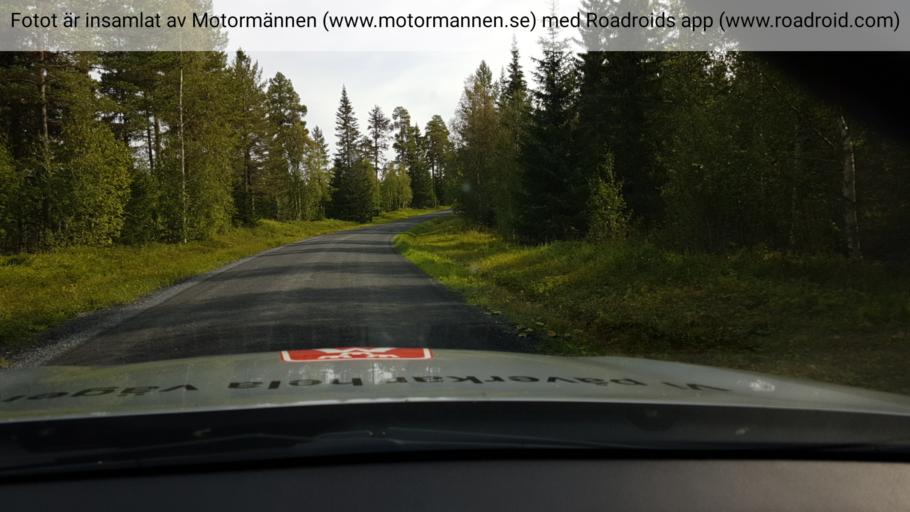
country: SE
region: Jaemtland
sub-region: Krokoms Kommun
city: Valla
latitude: 63.3663
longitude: 13.8915
